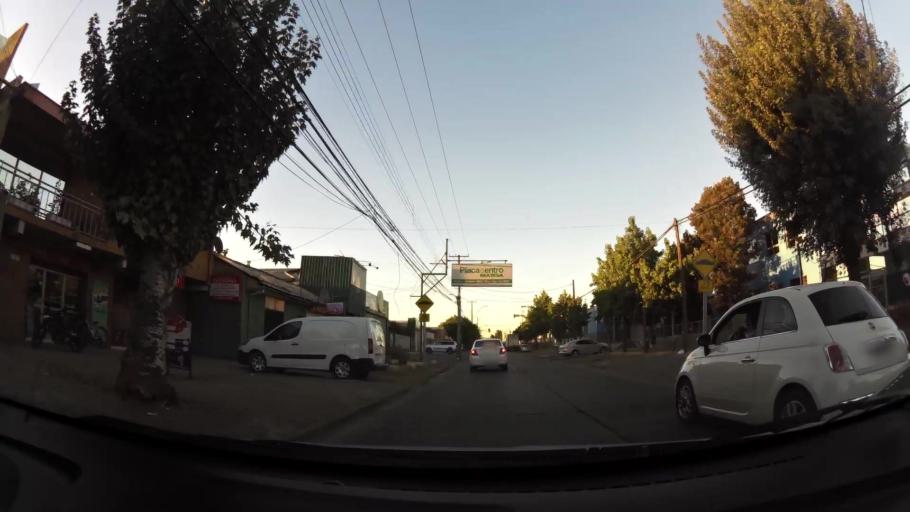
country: CL
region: Maule
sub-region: Provincia de Curico
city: Curico
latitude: -34.9796
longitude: -71.2395
